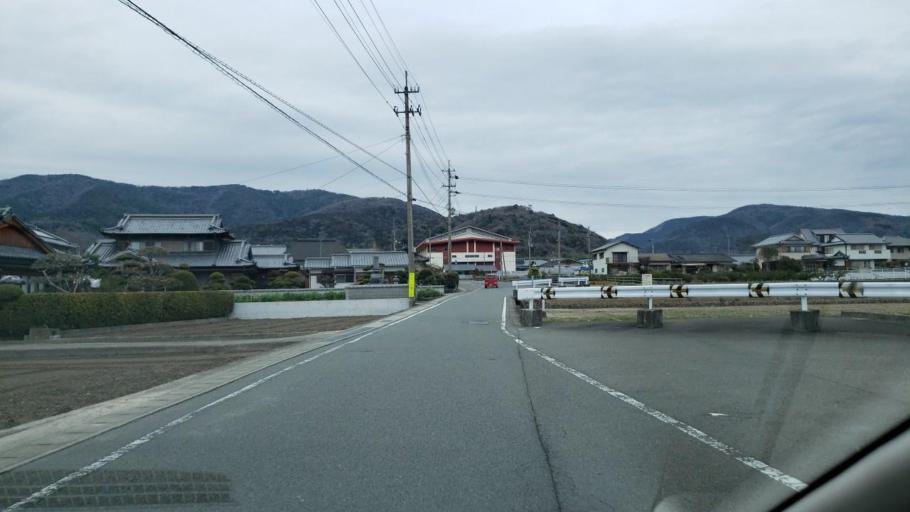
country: JP
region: Tokushima
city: Kamojimacho-jogejima
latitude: 34.1124
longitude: 134.3403
